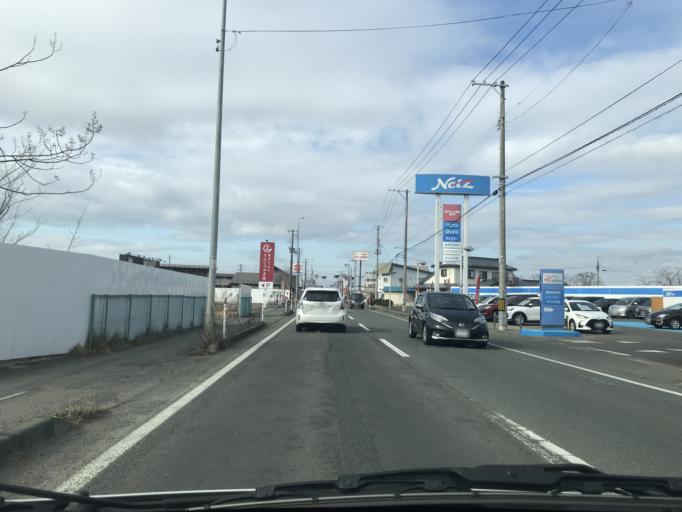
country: JP
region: Iwate
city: Hanamaki
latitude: 39.3883
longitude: 141.1247
